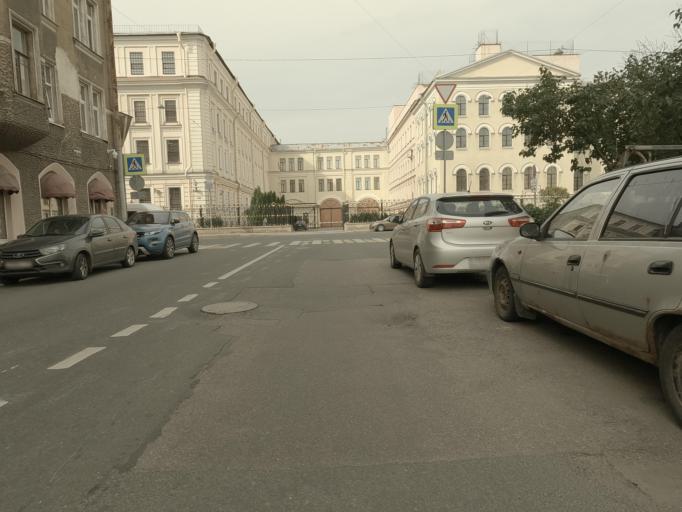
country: RU
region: St.-Petersburg
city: Admiralteisky
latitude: 59.9134
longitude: 30.2925
